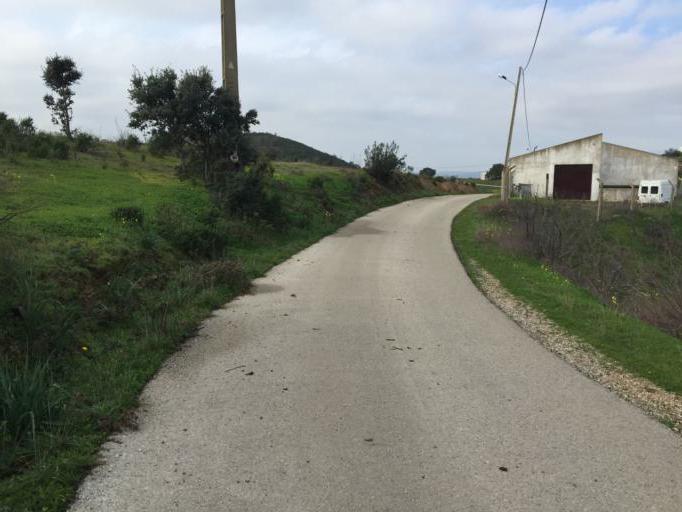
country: PT
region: Faro
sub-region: Castro Marim
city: Castro Marim
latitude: 37.3106
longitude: -7.5977
